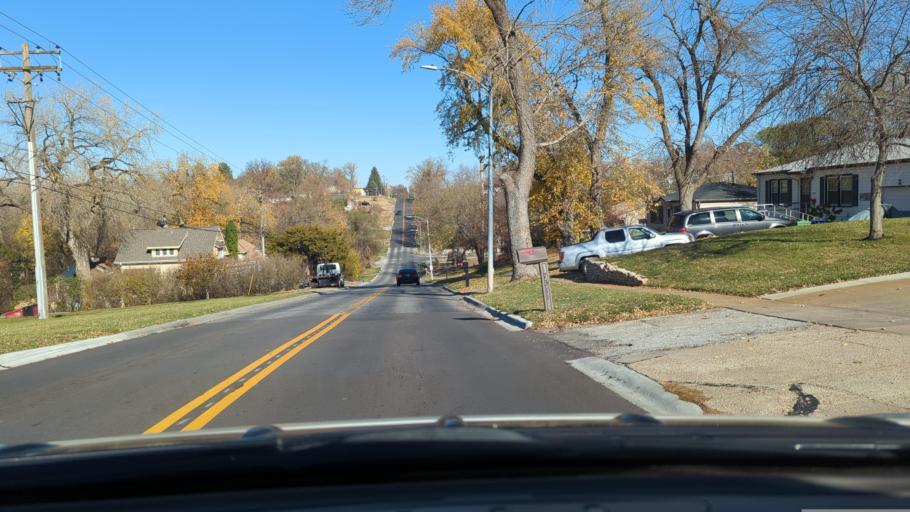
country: US
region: Nebraska
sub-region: Sarpy County
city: La Vista
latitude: 41.1866
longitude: -95.9770
